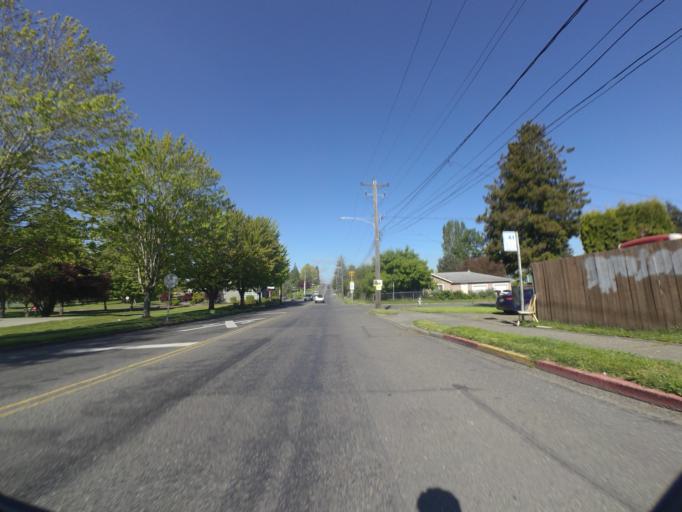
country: US
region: Washington
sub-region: Pierce County
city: Midland
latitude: 47.2065
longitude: -122.4241
